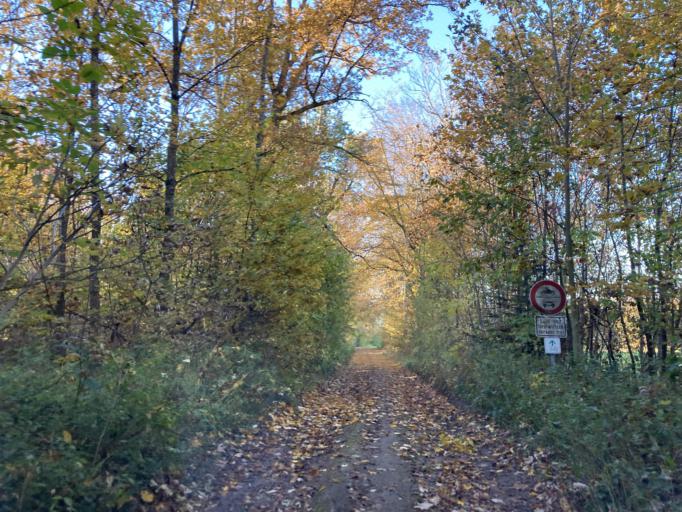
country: DE
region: Baden-Wuerttemberg
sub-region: Tuebingen Region
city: Ofterdingen
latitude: 48.4037
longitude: 9.0069
